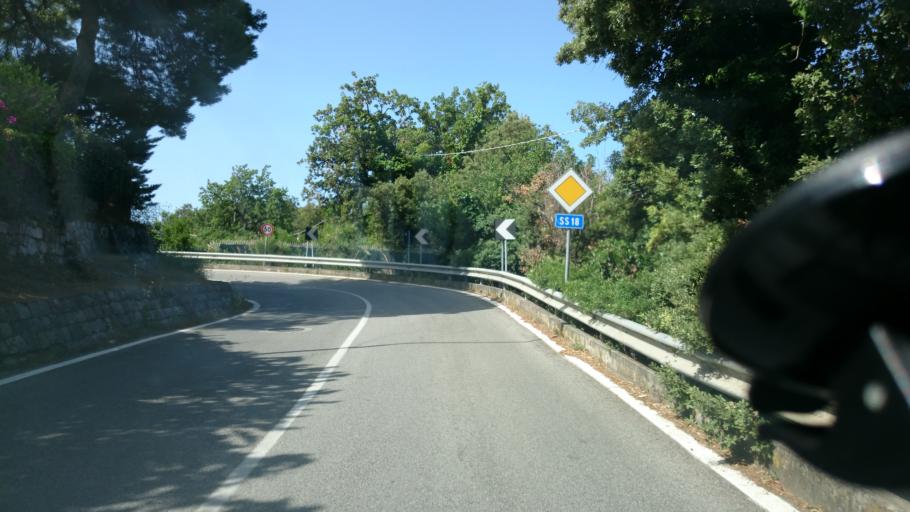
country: IT
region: Basilicate
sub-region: Provincia di Potenza
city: Maratea
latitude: 39.9977
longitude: 15.7042
